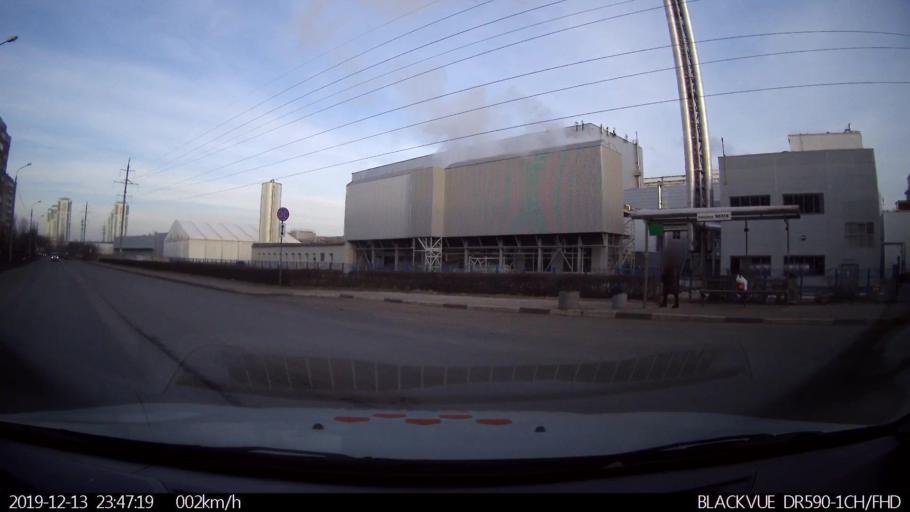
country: RU
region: Nizjnij Novgorod
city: Nizhniy Novgorod
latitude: 56.2932
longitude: 43.9523
